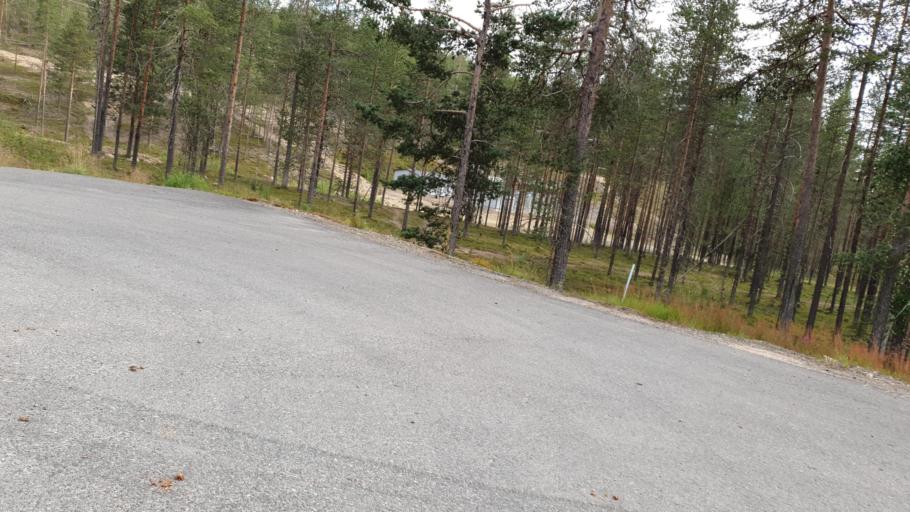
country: FI
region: Lapland
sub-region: Tunturi-Lappi
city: Kolari
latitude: 67.5932
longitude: 24.1216
